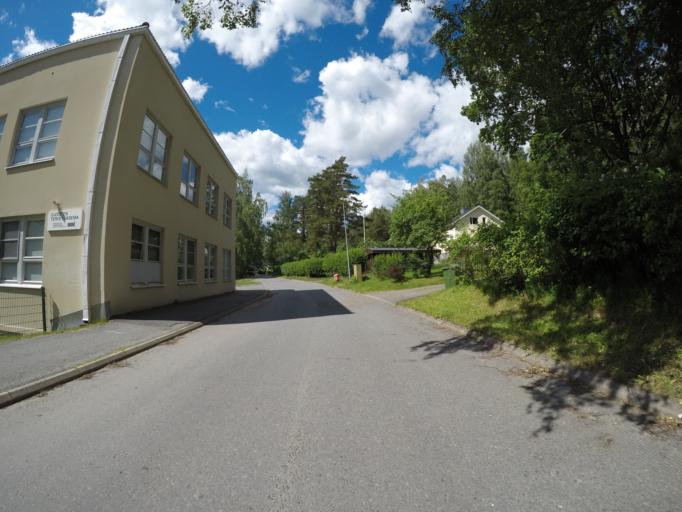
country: FI
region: Haeme
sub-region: Haemeenlinna
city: Haemeenlinna
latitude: 61.0119
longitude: 24.4379
